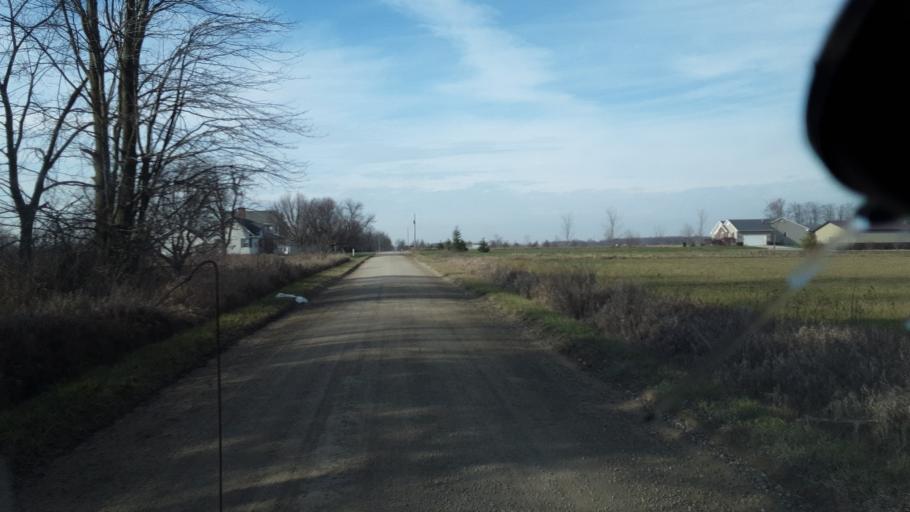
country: US
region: Ohio
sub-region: Defiance County
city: Hicksville
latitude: 41.2703
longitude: -84.8334
